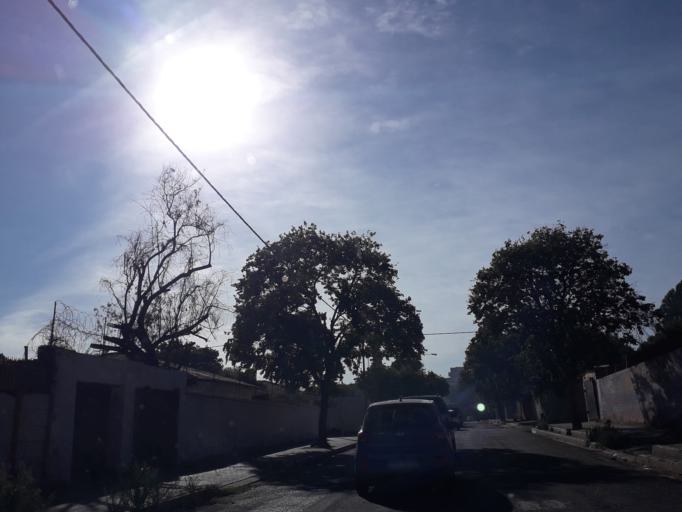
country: ZA
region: Gauteng
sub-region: City of Johannesburg Metropolitan Municipality
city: Johannesburg
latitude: -26.1820
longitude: 27.9809
